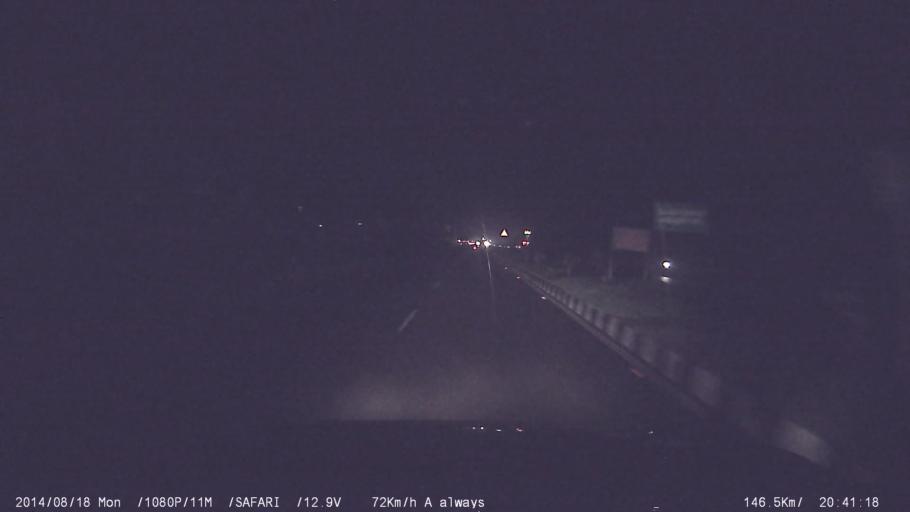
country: IN
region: Kerala
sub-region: Thrissur District
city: Kizhake Chalakudi
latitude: 10.3426
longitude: 76.3222
